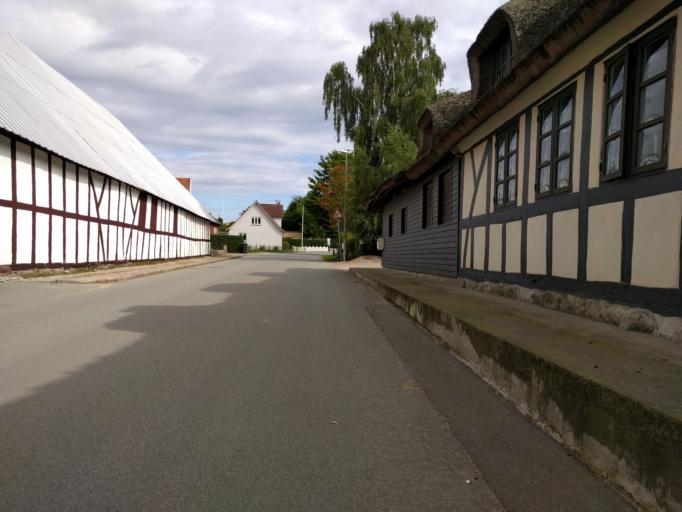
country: DK
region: South Denmark
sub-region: Kerteminde Kommune
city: Munkebo
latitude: 55.4666
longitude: 10.6063
